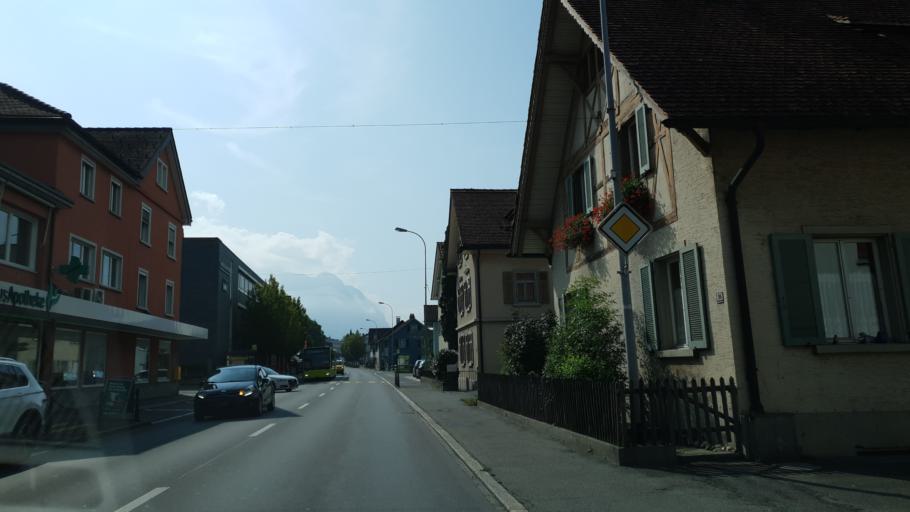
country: LI
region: Schaan
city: Schaan
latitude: 47.1615
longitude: 9.5087
